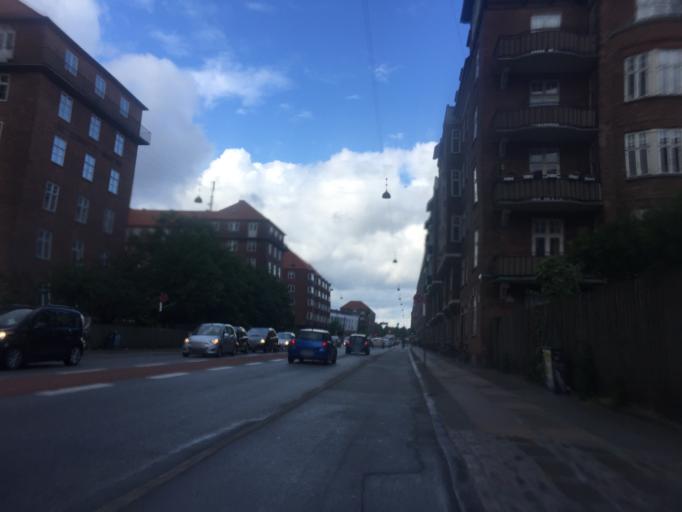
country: DK
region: Capital Region
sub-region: Kobenhavn
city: Christianshavn
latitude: 55.6645
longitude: 12.5945
